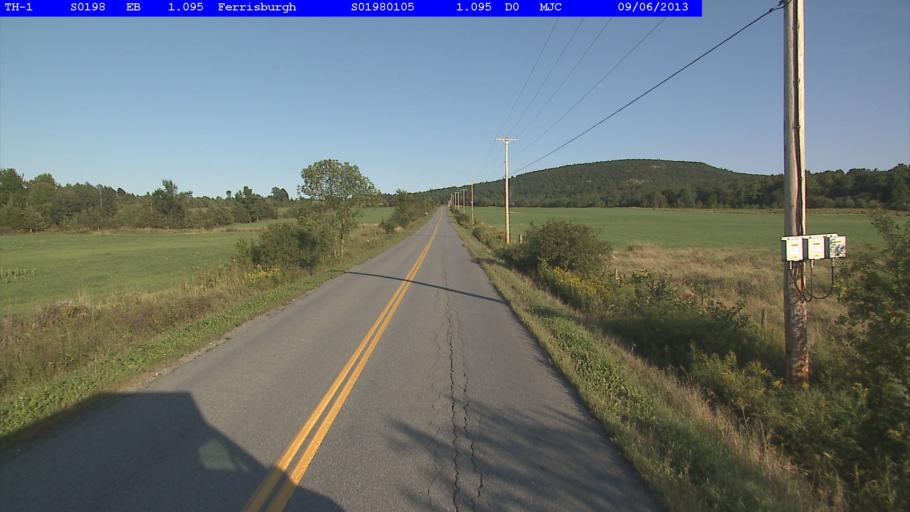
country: US
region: Vermont
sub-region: Addison County
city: Vergennes
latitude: 44.2578
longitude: -73.2068
